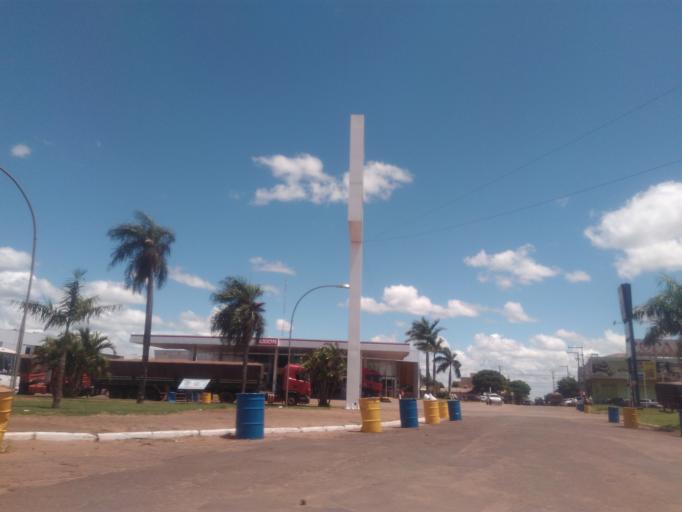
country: PY
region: Amambay
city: Pedro Juan Caballero
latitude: -22.5554
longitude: -55.7162
